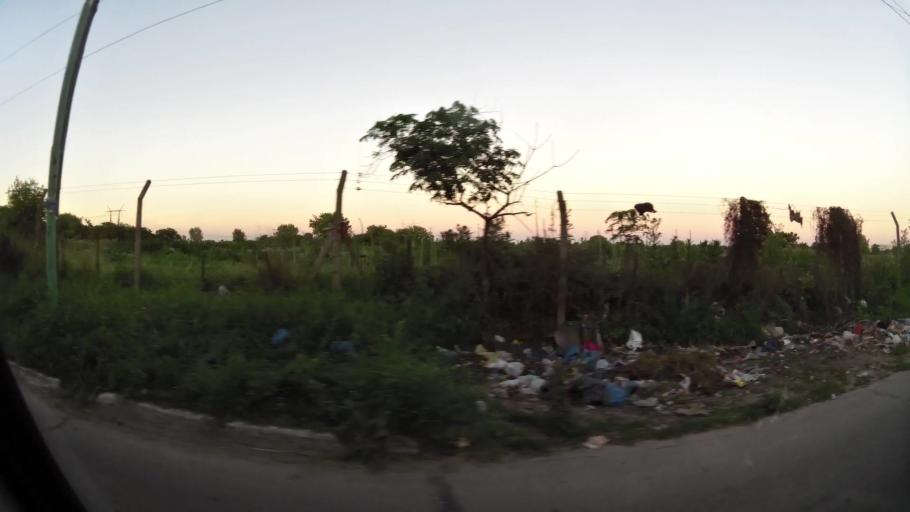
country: AR
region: Buenos Aires
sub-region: Partido de Quilmes
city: Quilmes
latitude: -34.7993
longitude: -58.1871
